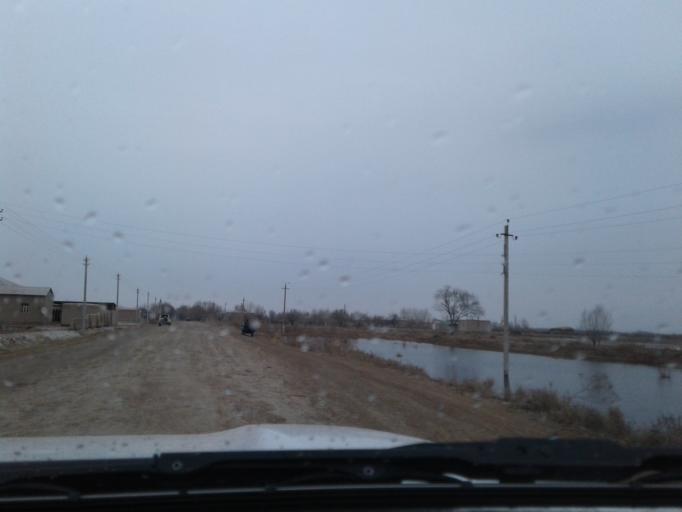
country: UZ
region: Karakalpakstan
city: Shumanay Shahri
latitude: 42.2782
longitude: 58.6509
